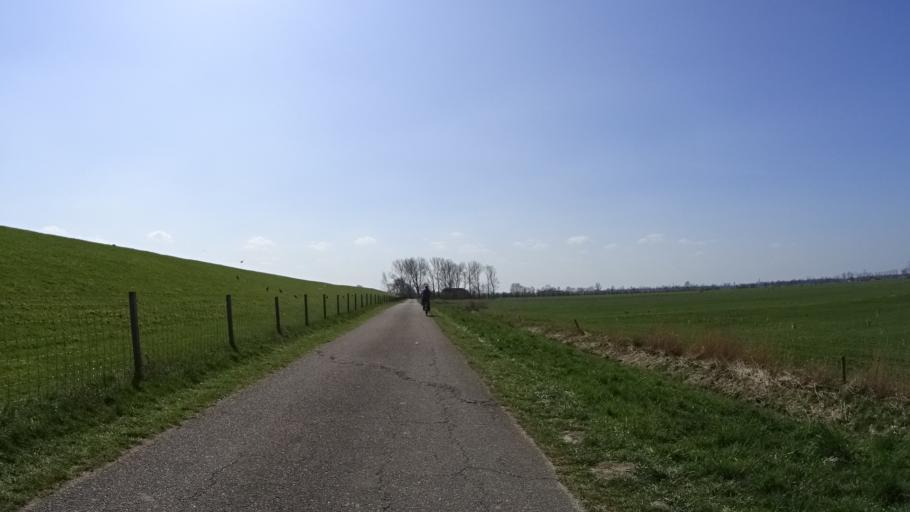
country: DE
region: Lower Saxony
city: Weener
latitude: 53.1373
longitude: 7.3652
